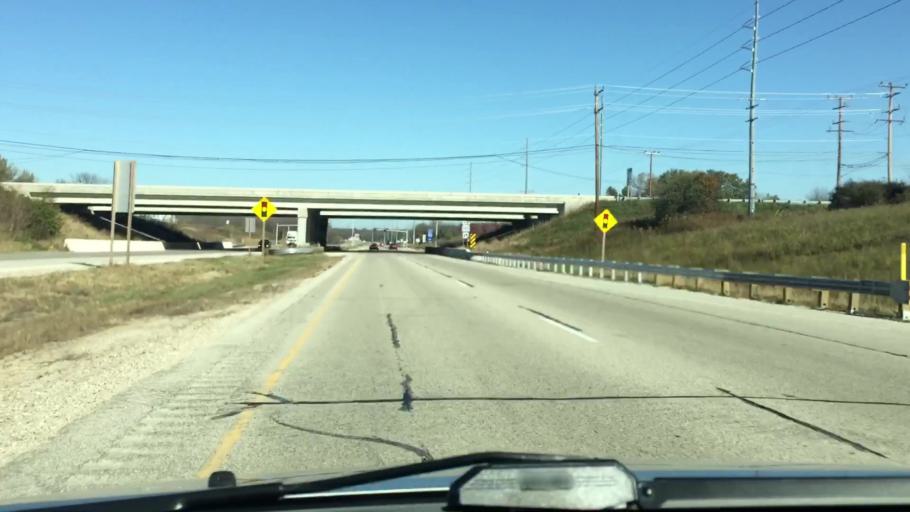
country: US
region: Wisconsin
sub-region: Waukesha County
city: Sussex
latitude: 43.0820
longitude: -88.2055
